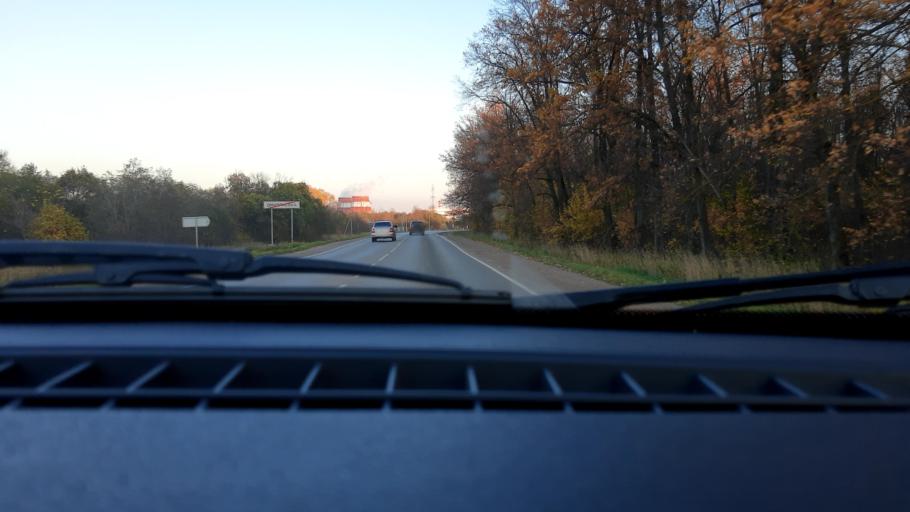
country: RU
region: Bashkortostan
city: Mikhaylovka
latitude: 54.8086
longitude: 55.8159
